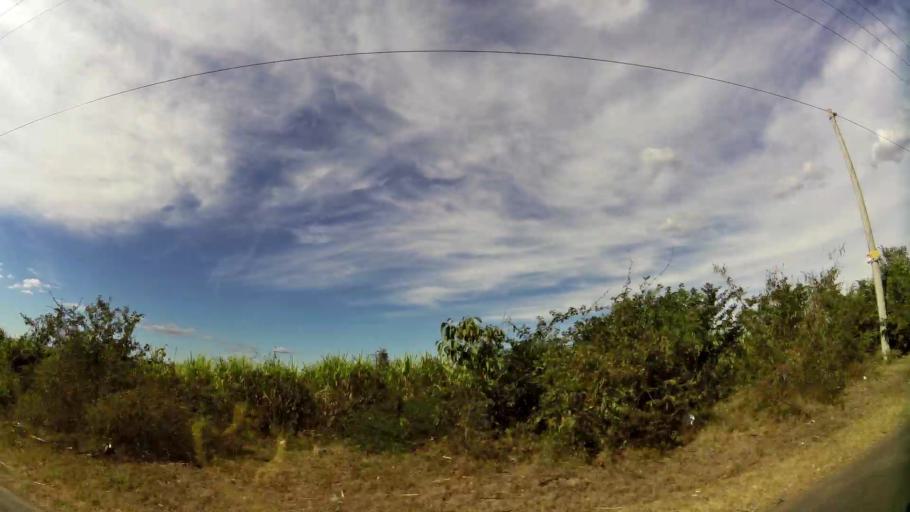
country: SV
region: San Salvador
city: Aguilares
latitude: 13.9592
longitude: -89.1363
